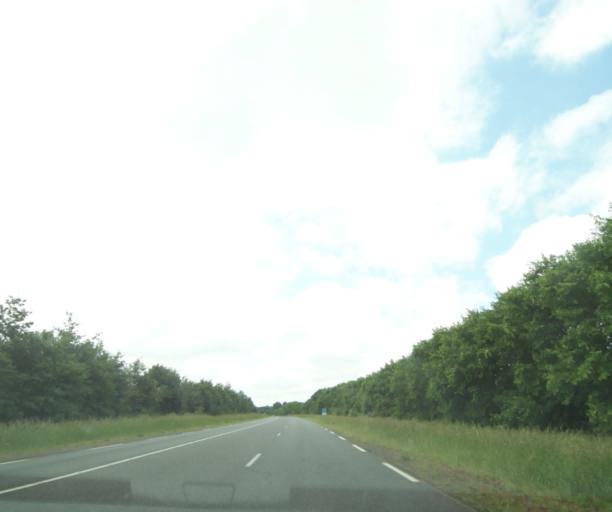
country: FR
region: Poitou-Charentes
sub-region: Departement des Deux-Sevres
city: Airvault
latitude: 46.8162
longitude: -0.2076
